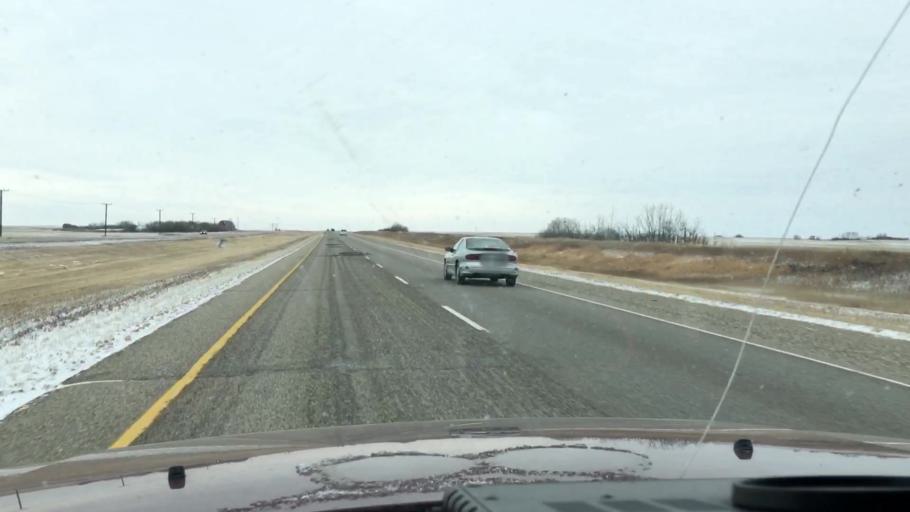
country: CA
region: Saskatchewan
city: Watrous
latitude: 51.4251
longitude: -106.1965
